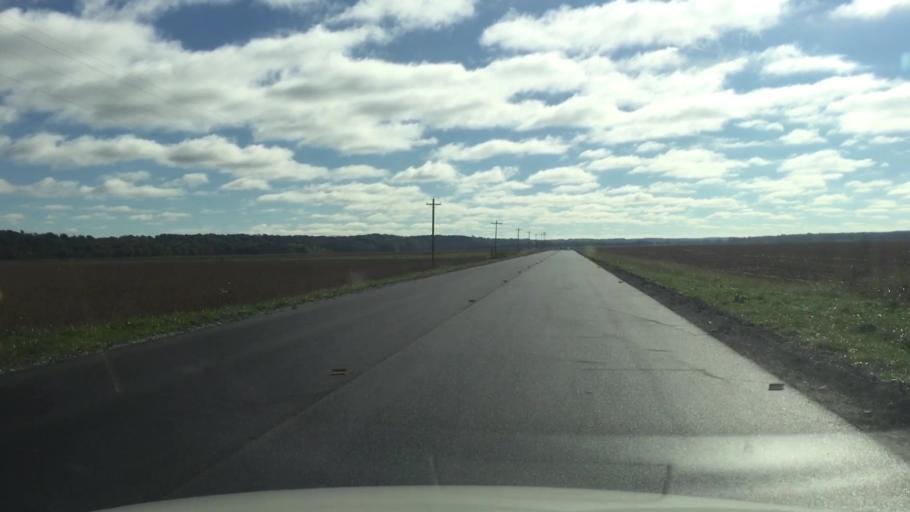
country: US
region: Missouri
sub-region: Howard County
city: New Franklin
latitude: 38.9943
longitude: -92.6552
